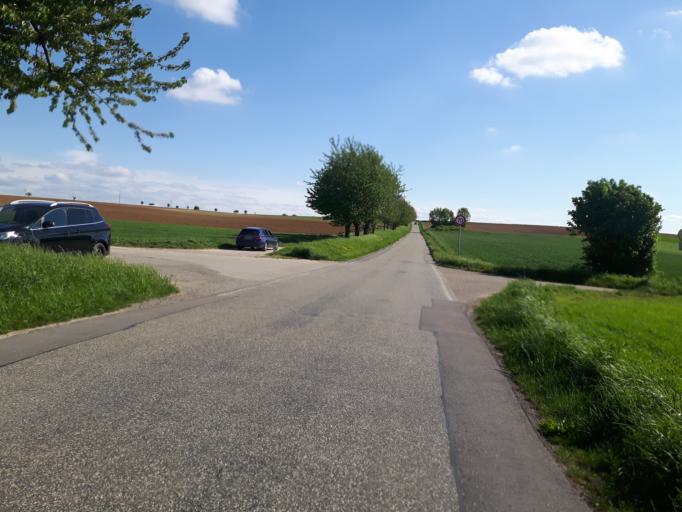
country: DE
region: Baden-Wuerttemberg
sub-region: Regierungsbezirk Stuttgart
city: Gundelsheim
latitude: 49.2707
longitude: 9.1602
